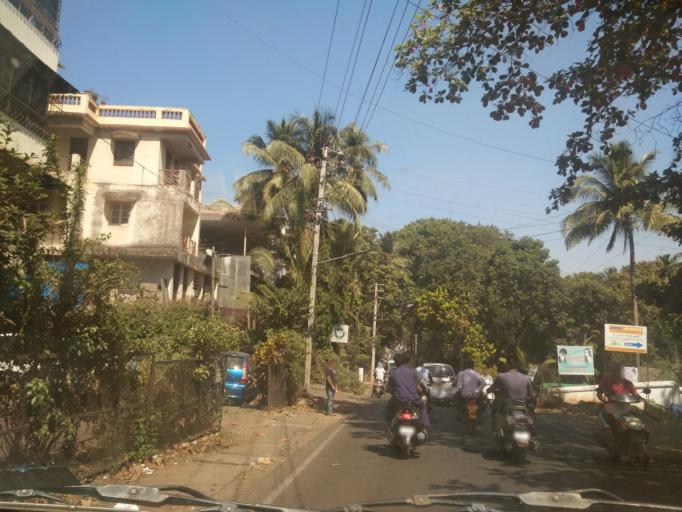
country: IN
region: Goa
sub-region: North Goa
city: Mapuca
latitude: 15.5954
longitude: 73.8149
